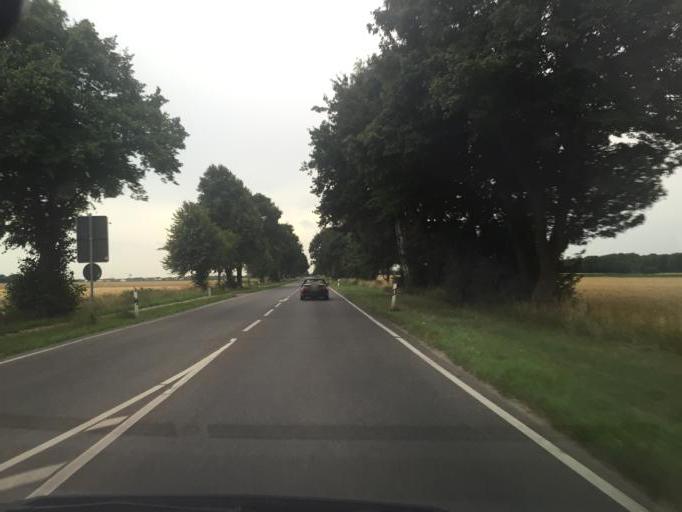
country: DE
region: North Rhine-Westphalia
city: Erkelenz
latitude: 51.1077
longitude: 6.3269
